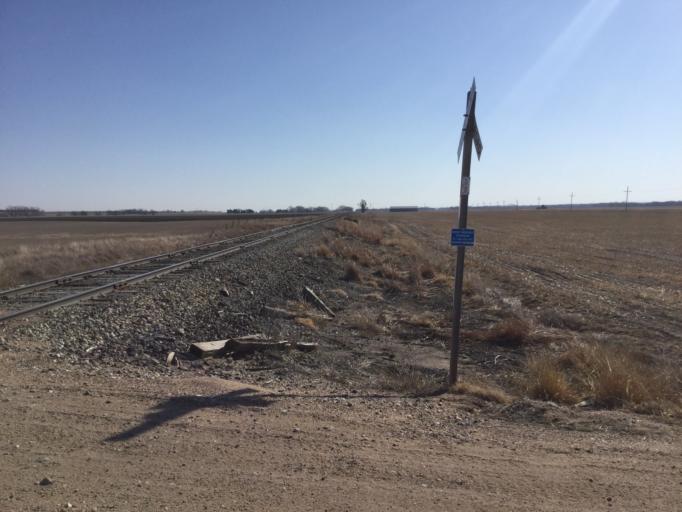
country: US
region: Kansas
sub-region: Rush County
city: La Crosse
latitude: 38.4663
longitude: -99.2720
